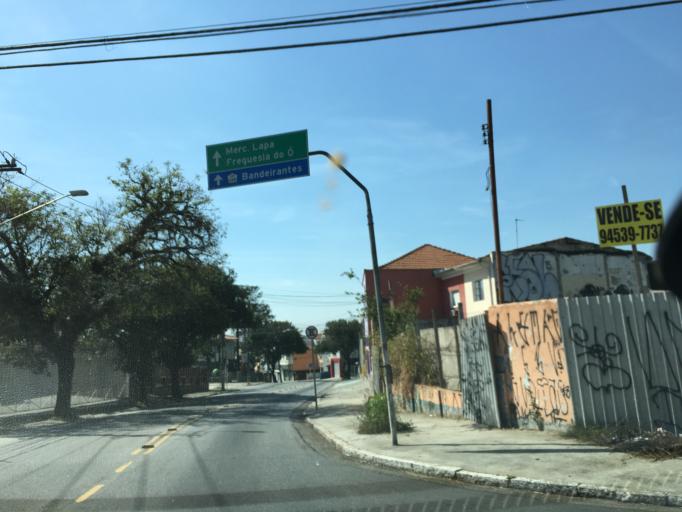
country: BR
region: Sao Paulo
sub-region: Sao Paulo
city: Sao Paulo
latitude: -23.5287
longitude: -46.7106
